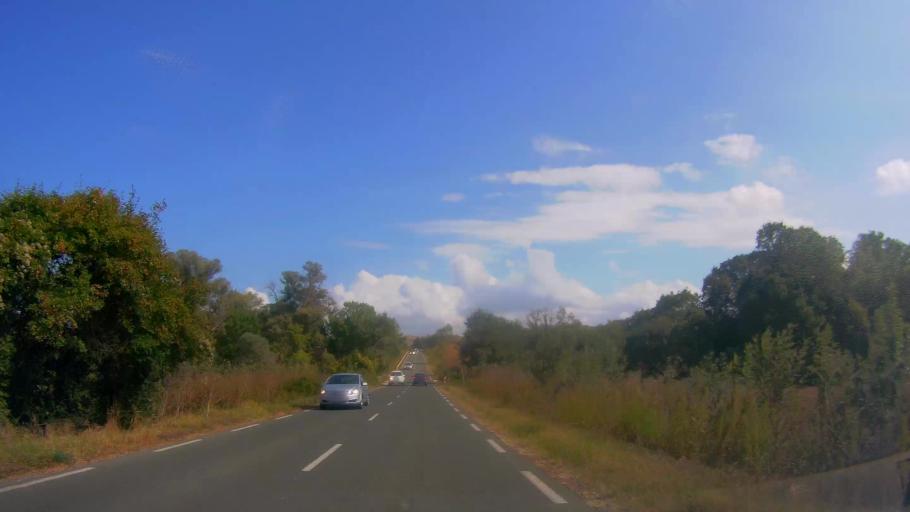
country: BG
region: Burgas
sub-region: Obshtina Burgas
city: Burgas
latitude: 42.4761
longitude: 27.3569
